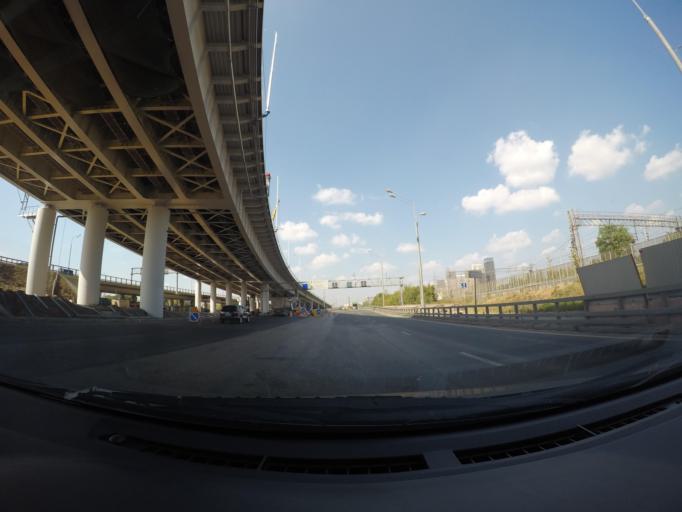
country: RU
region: Moscow
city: Likhobory
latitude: 55.8501
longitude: 37.5514
